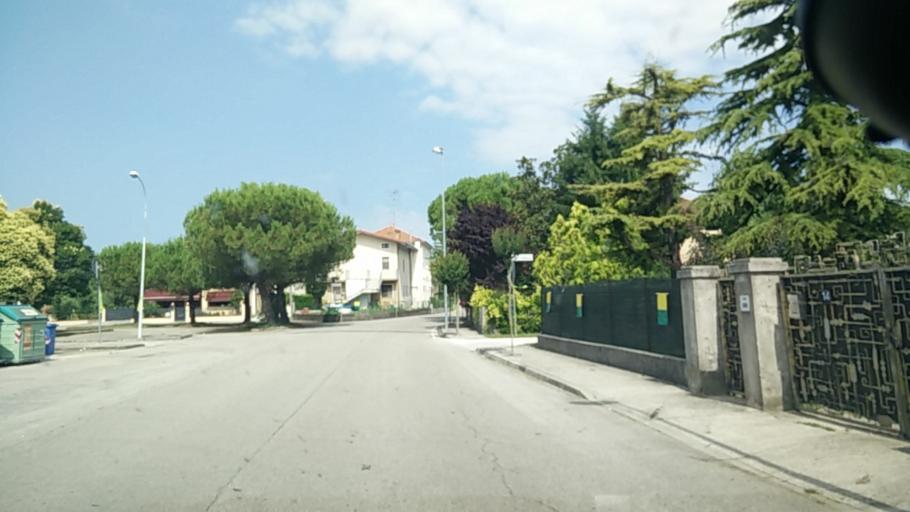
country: IT
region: Friuli Venezia Giulia
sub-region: Provincia di Pordenone
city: Puia-Villanova
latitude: 45.8439
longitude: 12.5656
